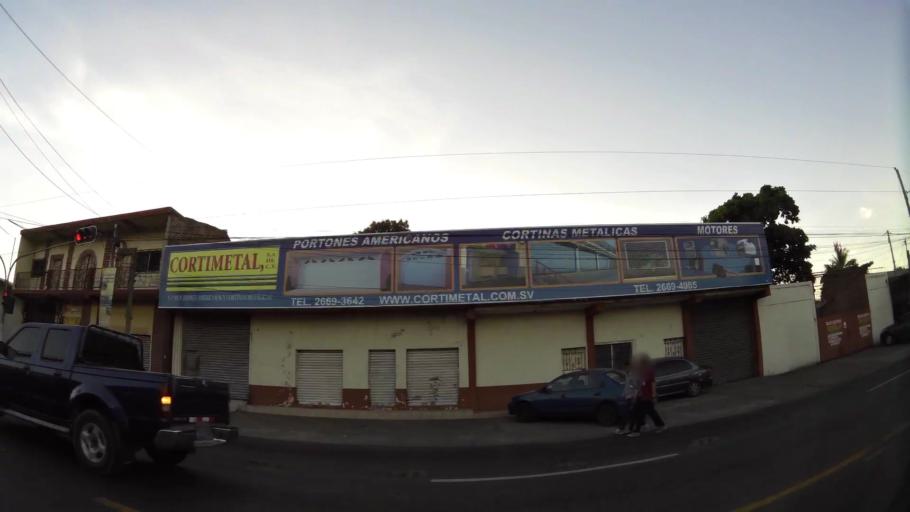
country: SV
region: San Miguel
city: San Miguel
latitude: 13.4920
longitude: -88.1717
